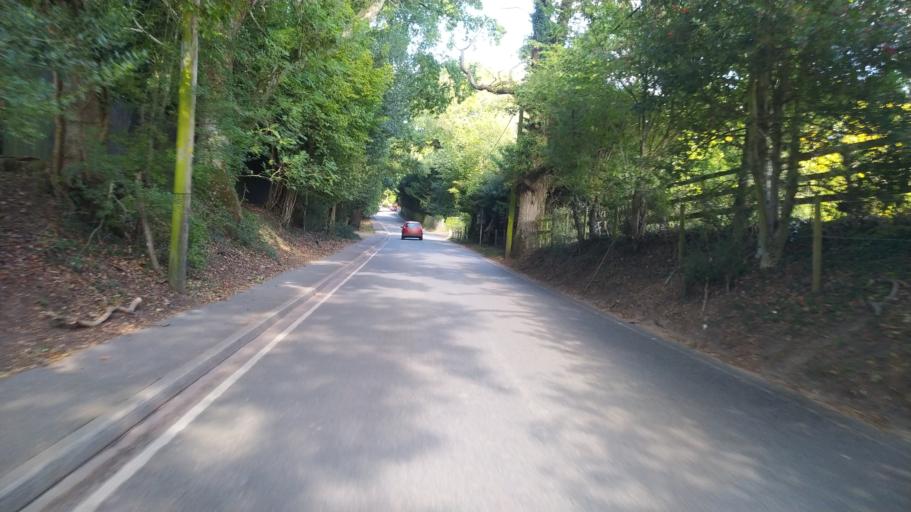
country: GB
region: England
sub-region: Hampshire
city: Bransgore
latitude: 50.8314
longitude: -1.7102
